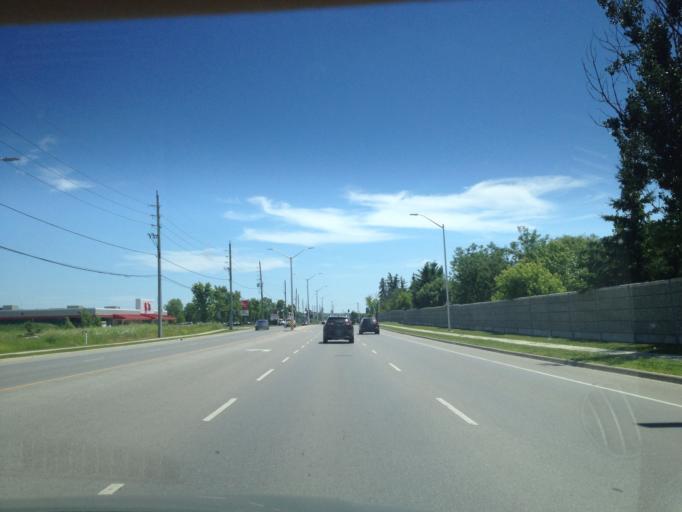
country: CA
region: Ontario
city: London
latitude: 42.9968
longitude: -81.3313
